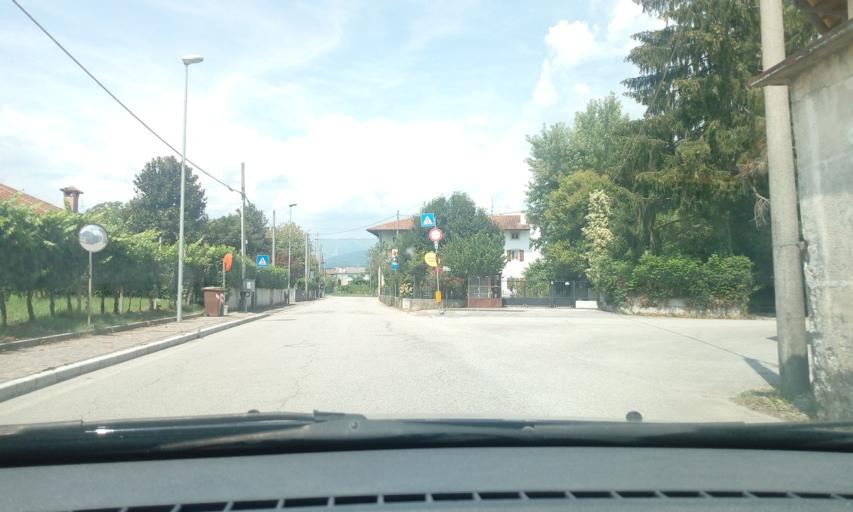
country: IT
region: Friuli Venezia Giulia
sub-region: Provincia di Udine
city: Faedis
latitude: 46.1370
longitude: 13.3182
